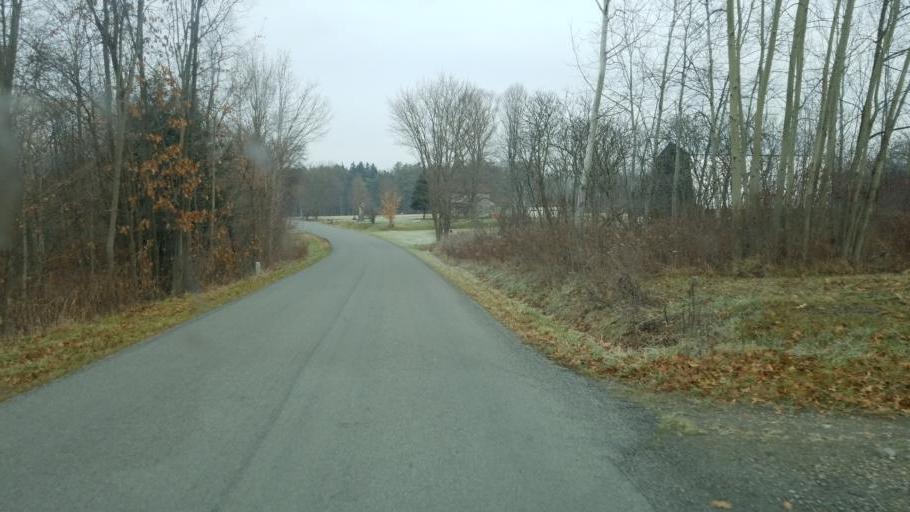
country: US
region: Pennsylvania
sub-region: Crawford County
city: Cochranton
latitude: 41.5174
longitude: -80.1214
